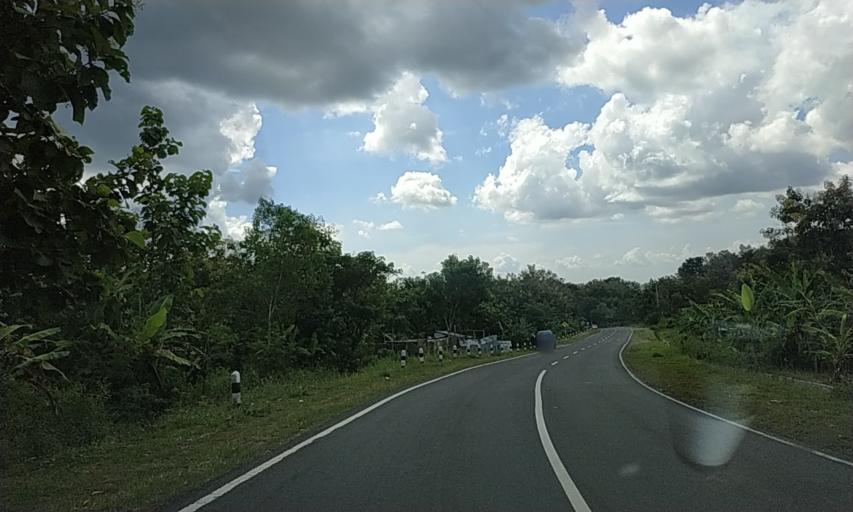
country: ID
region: East Java
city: Krajan
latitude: -8.0443
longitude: 110.9463
